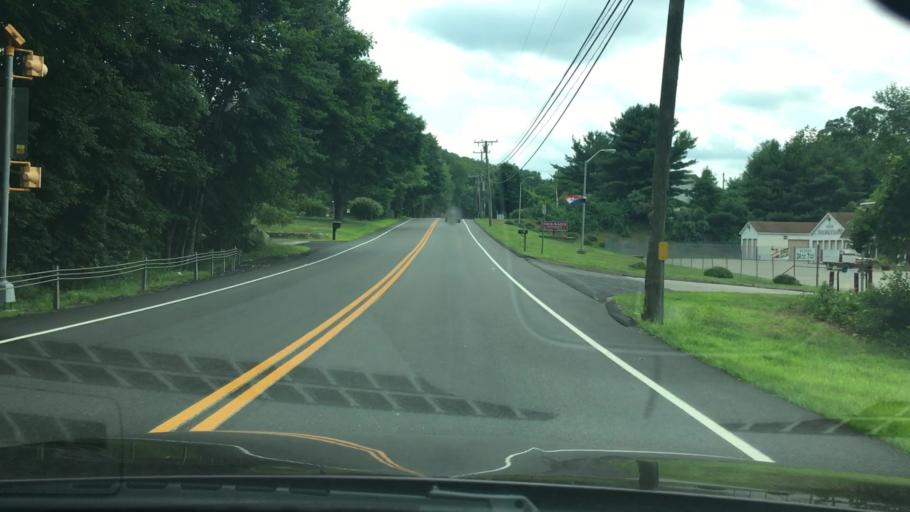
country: US
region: Connecticut
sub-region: Tolland County
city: Storrs
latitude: 41.8491
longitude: -72.3029
